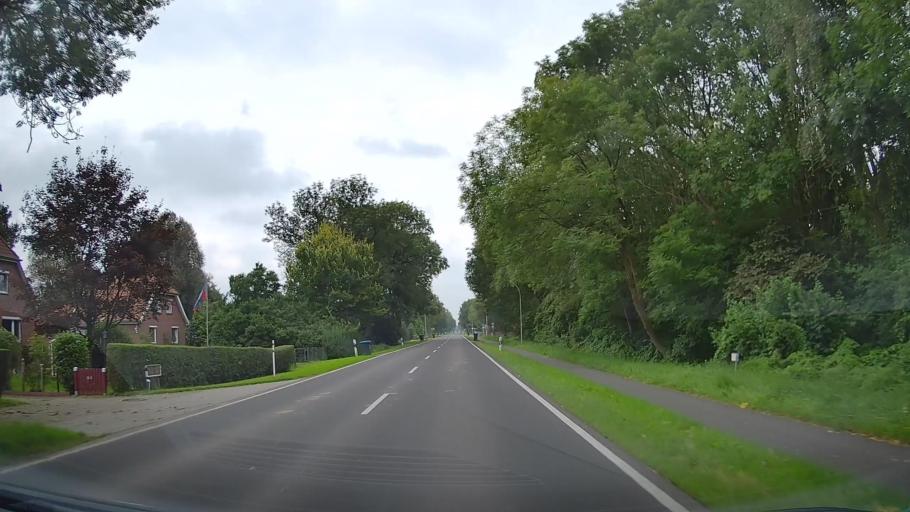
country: DE
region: Lower Saxony
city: Drochtersen
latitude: 53.7305
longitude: 9.3516
